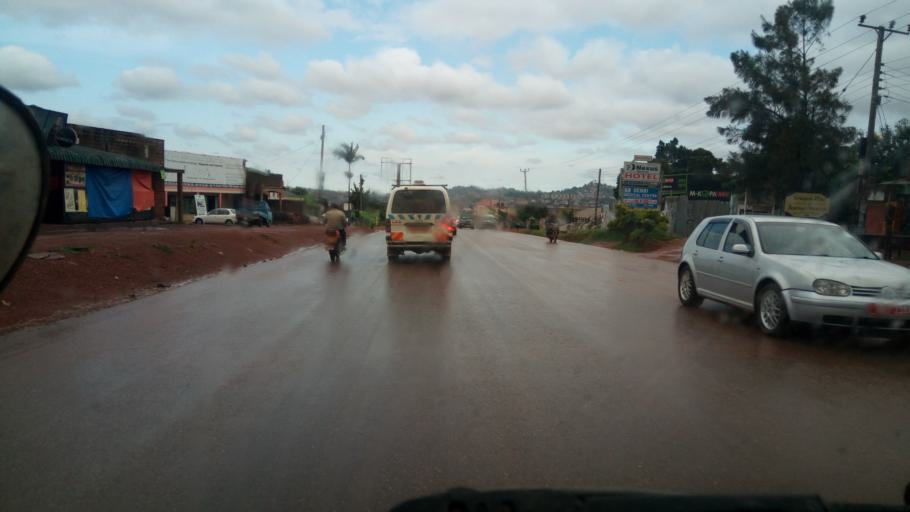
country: UG
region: Central Region
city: Kampala Central Division
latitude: 0.3569
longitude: 32.5337
